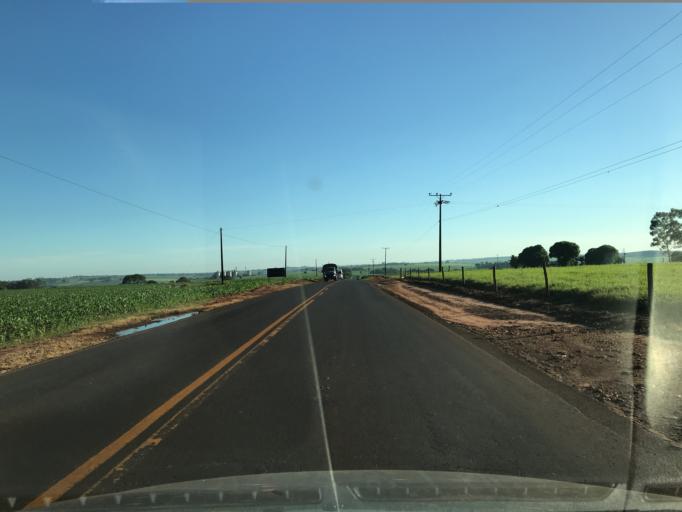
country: BR
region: Parana
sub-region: Palotina
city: Palotina
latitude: -24.1346
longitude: -53.8554
